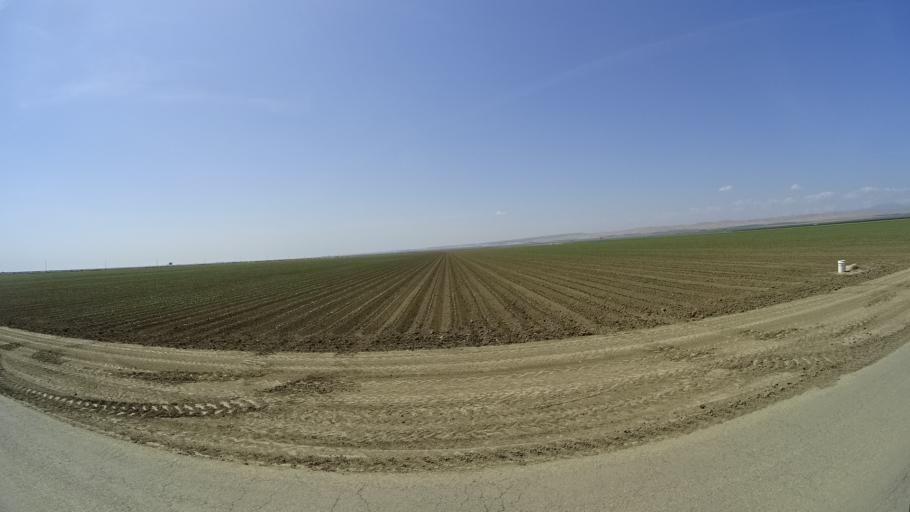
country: US
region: California
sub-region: Kings County
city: Kettleman City
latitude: 36.0943
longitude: -119.9721
